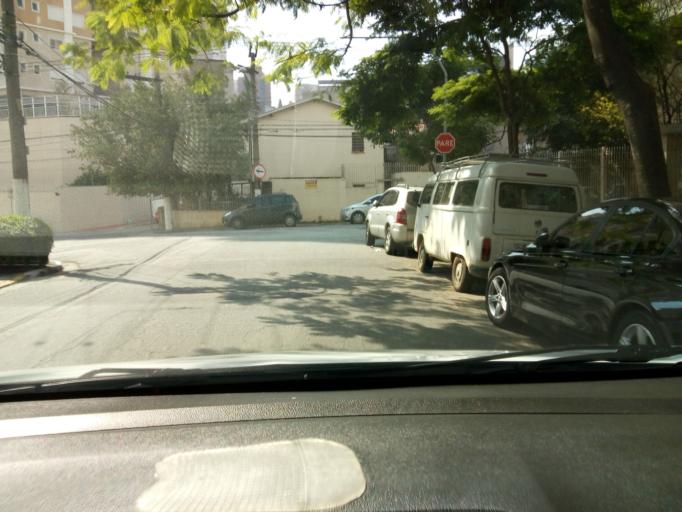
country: BR
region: Sao Paulo
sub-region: Sao Paulo
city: Sao Paulo
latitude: -23.5836
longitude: -46.6448
